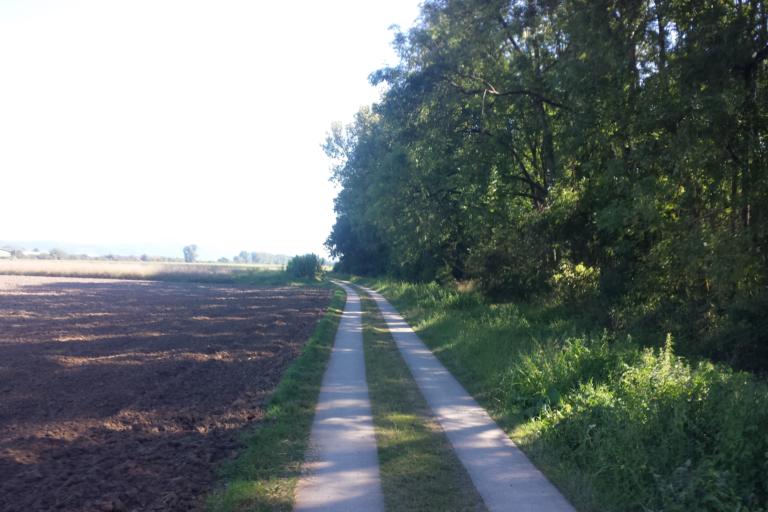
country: DE
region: Hesse
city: Viernheim
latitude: 49.5803
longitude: 8.5956
